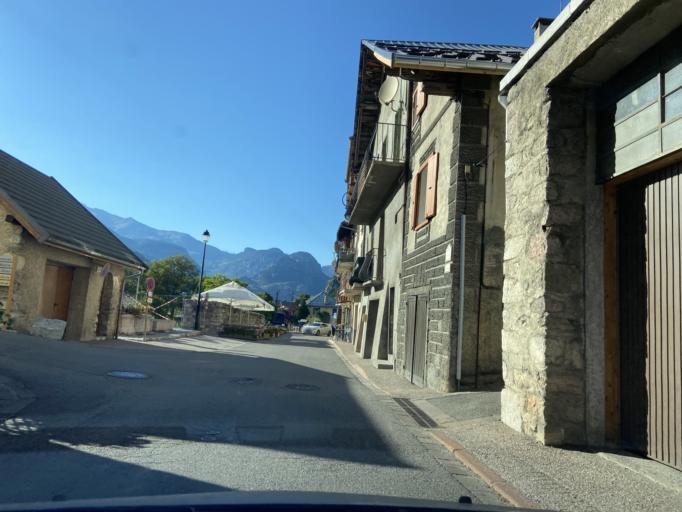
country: FR
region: Provence-Alpes-Cote d'Azur
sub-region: Departement des Hautes-Alpes
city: Guillestre
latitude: 44.7071
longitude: 6.6075
